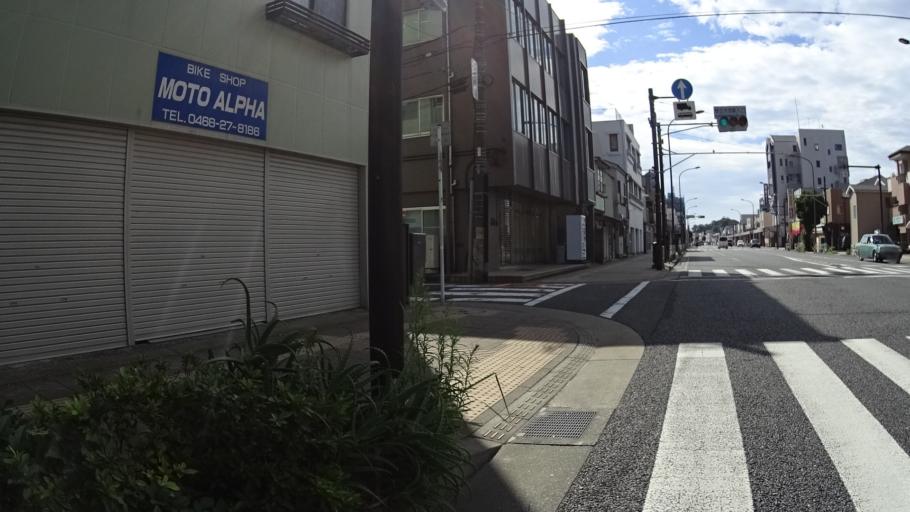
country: JP
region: Kanagawa
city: Yokosuka
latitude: 35.2718
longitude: 139.6777
